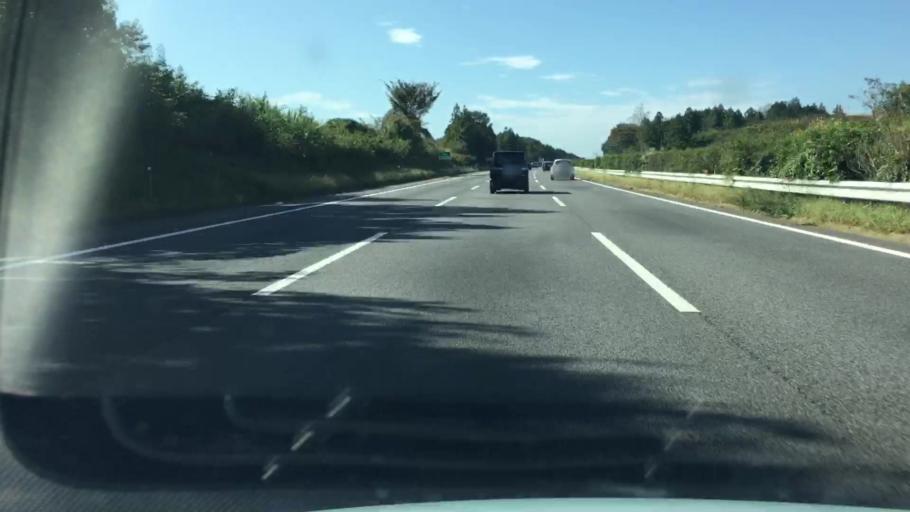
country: JP
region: Ibaraki
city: Ishioka
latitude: 36.1404
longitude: 140.2060
